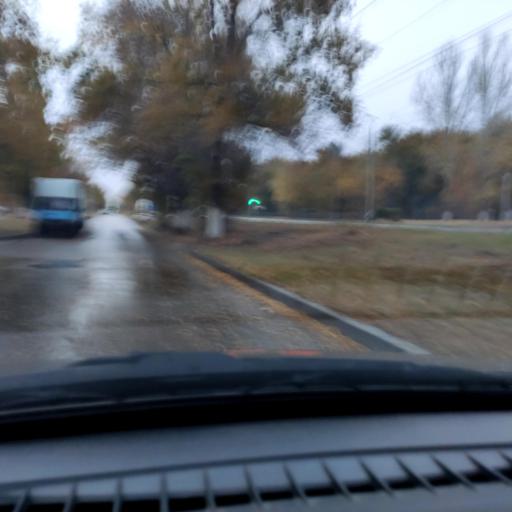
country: RU
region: Samara
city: Zhigulevsk
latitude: 53.4781
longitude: 49.4859
